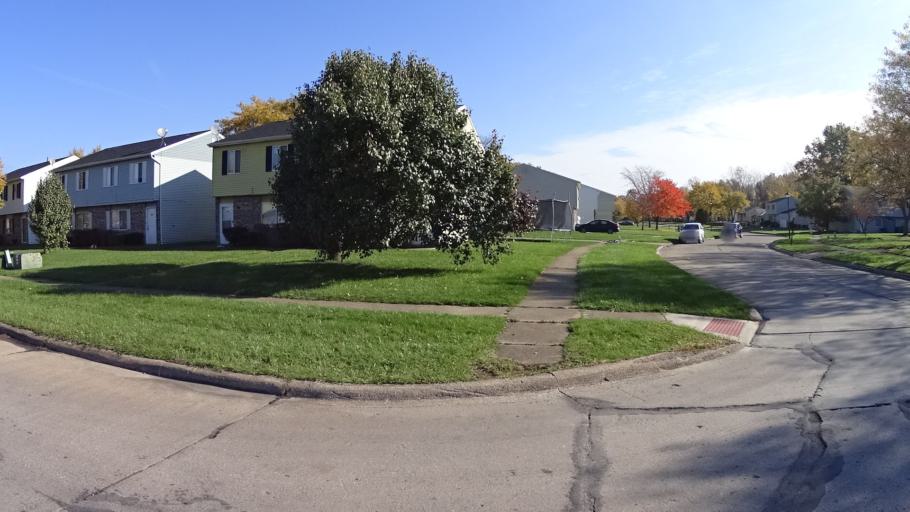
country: US
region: Ohio
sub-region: Lorain County
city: Lorain
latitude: 41.4673
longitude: -82.1527
